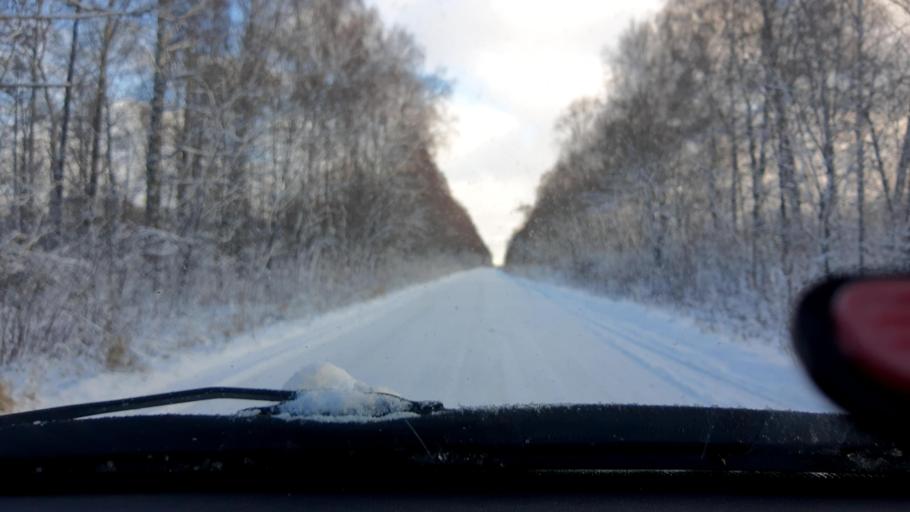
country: RU
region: Bashkortostan
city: Iglino
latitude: 54.8407
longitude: 56.4563
